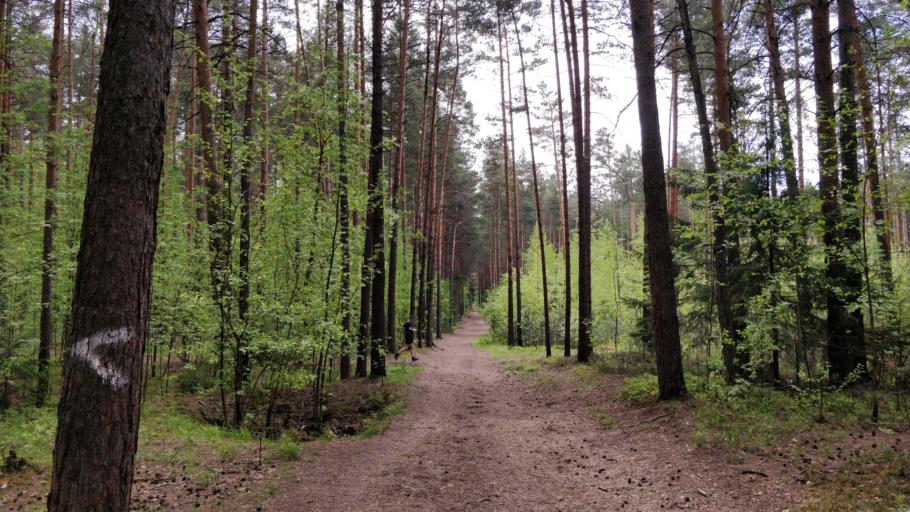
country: RU
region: Perm
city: Kondratovo
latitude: 57.9799
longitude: 56.1363
